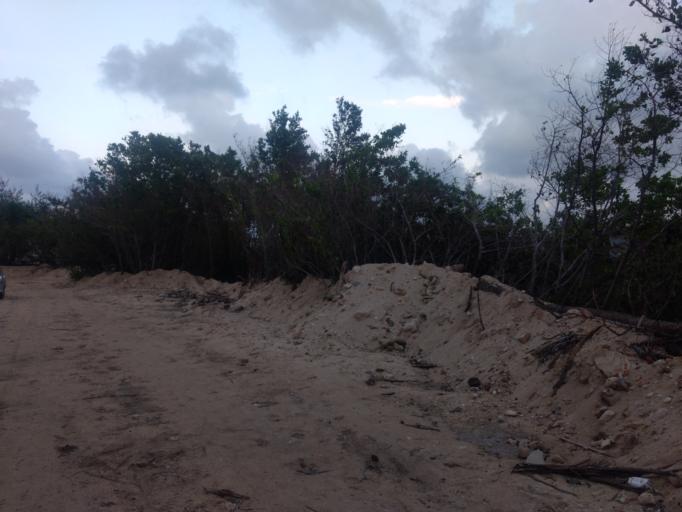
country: CU
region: Artemisa
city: Bauta
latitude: 23.0810
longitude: -82.5105
